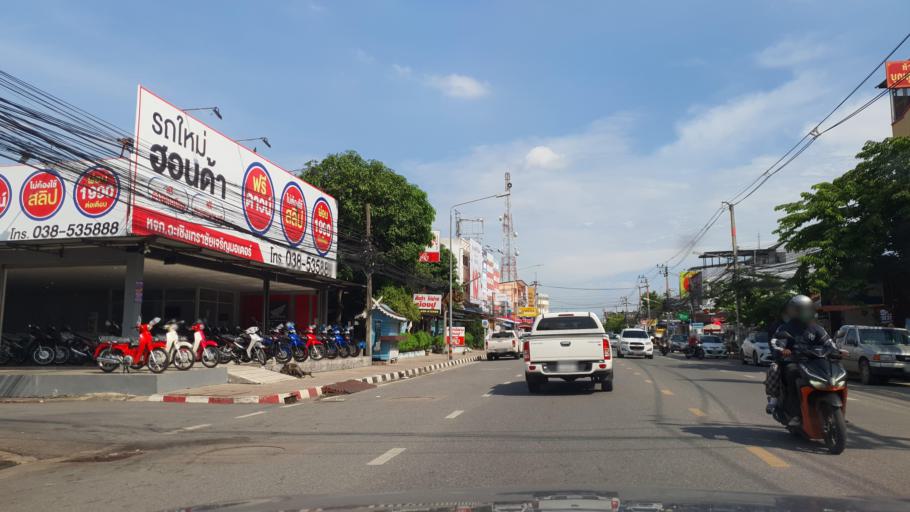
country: TH
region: Chachoengsao
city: Chachoengsao
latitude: 13.6836
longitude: 101.0664
